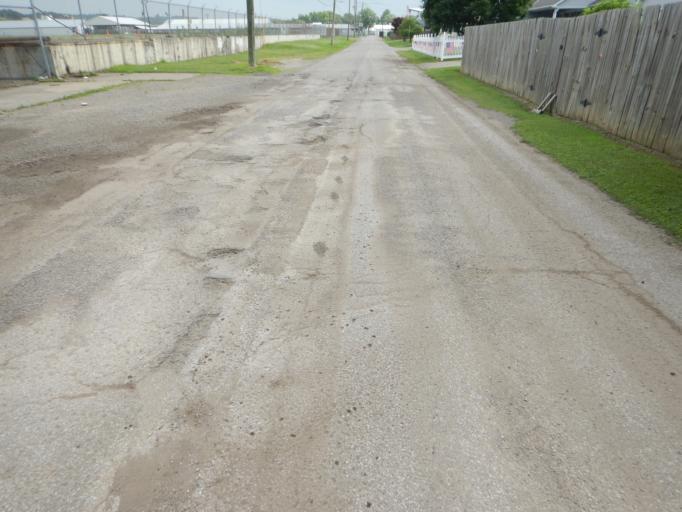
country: US
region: Ohio
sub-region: Muskingum County
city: Zanesville
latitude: 39.9193
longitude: -82.0231
